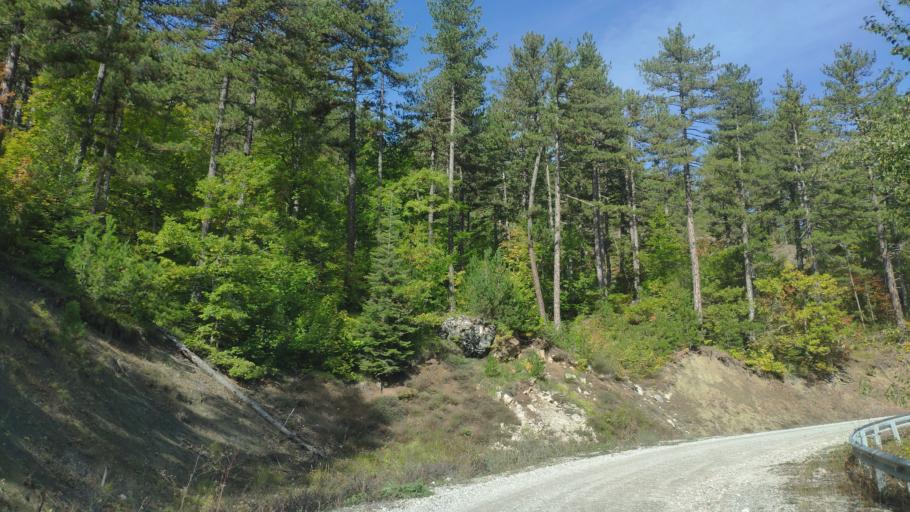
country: AL
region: Korce
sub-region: Rrethi i Devollit
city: Miras
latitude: 40.4154
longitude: 20.8707
